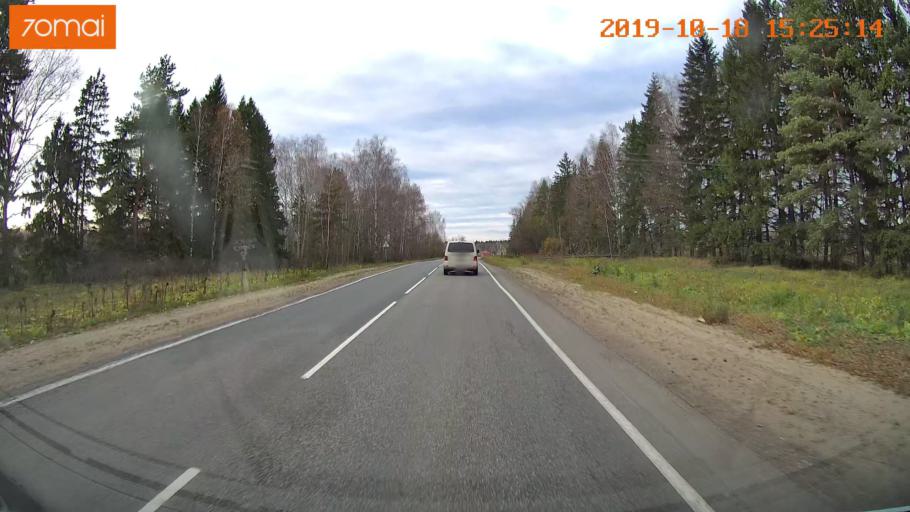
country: RU
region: Vladimir
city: Anopino
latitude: 55.7399
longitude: 40.7089
